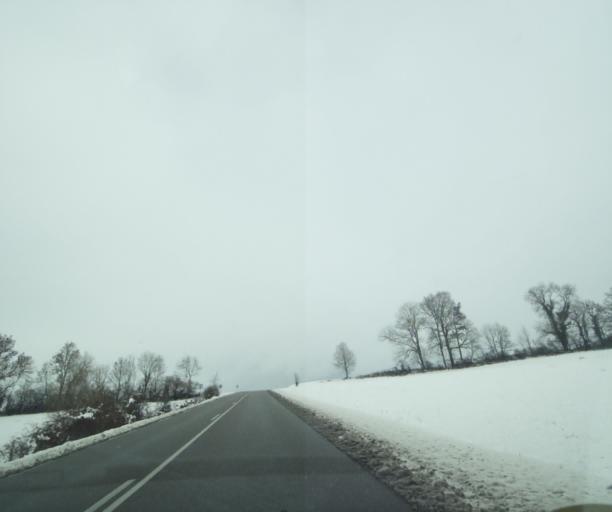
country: FR
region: Champagne-Ardenne
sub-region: Departement de la Haute-Marne
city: Montier-en-Der
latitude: 48.4516
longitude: 4.7407
